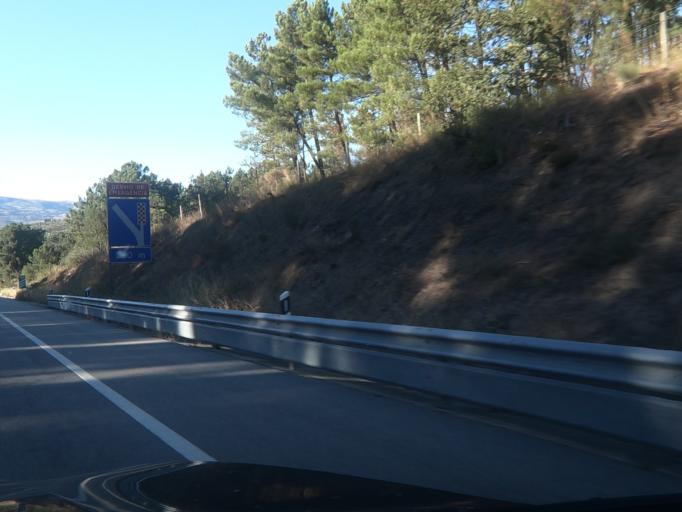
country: PT
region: Vila Real
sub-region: Vila Real
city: Vila Real
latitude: 41.3239
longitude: -7.6685
